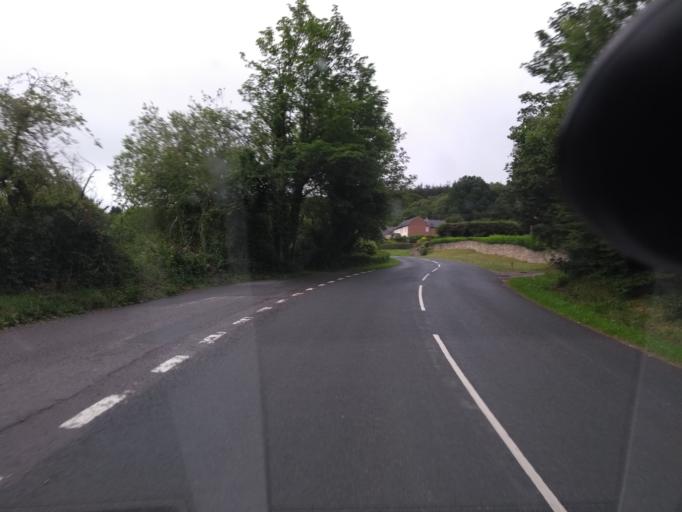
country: GB
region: England
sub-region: Somerset
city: Taunton
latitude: 50.9518
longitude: -3.1284
